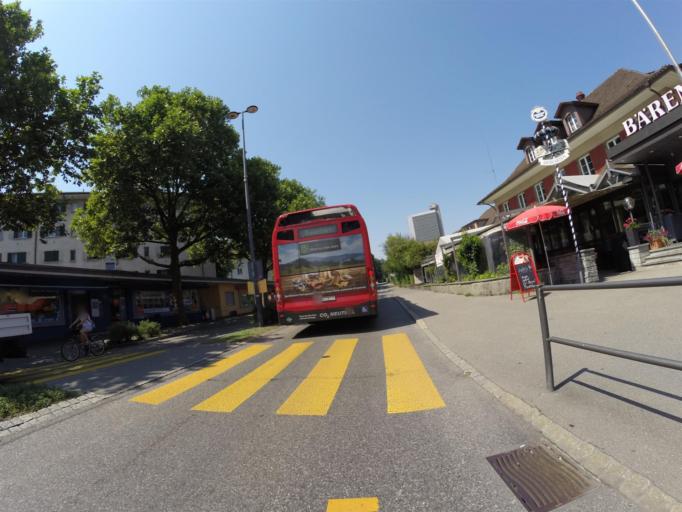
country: CH
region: Bern
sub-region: Bern-Mittelland District
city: Bolligen
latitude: 46.9557
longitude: 7.4811
